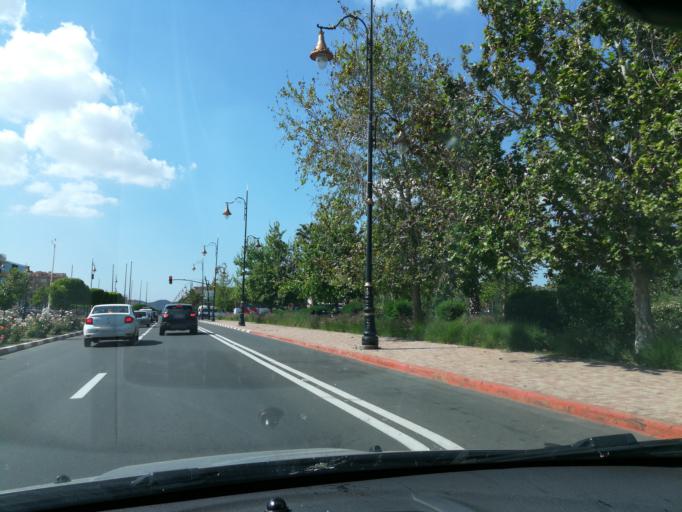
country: MA
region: Marrakech-Tensift-Al Haouz
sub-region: Marrakech
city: Marrakesh
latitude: 31.6170
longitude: -8.0073
